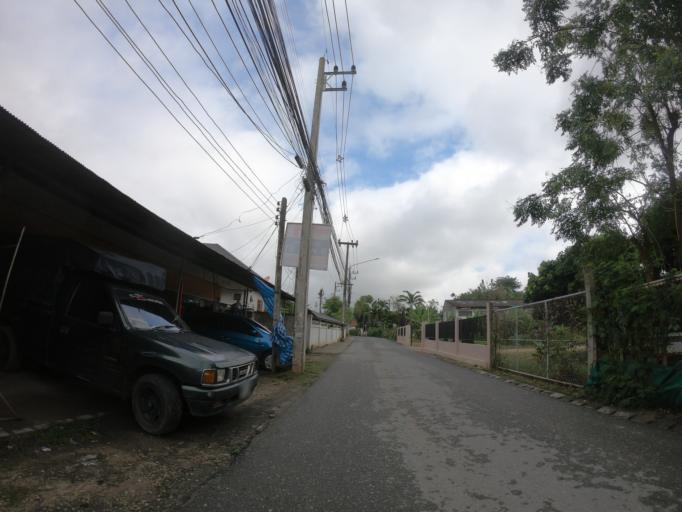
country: TH
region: Chiang Mai
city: Chiang Mai
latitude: 18.8156
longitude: 99.0067
